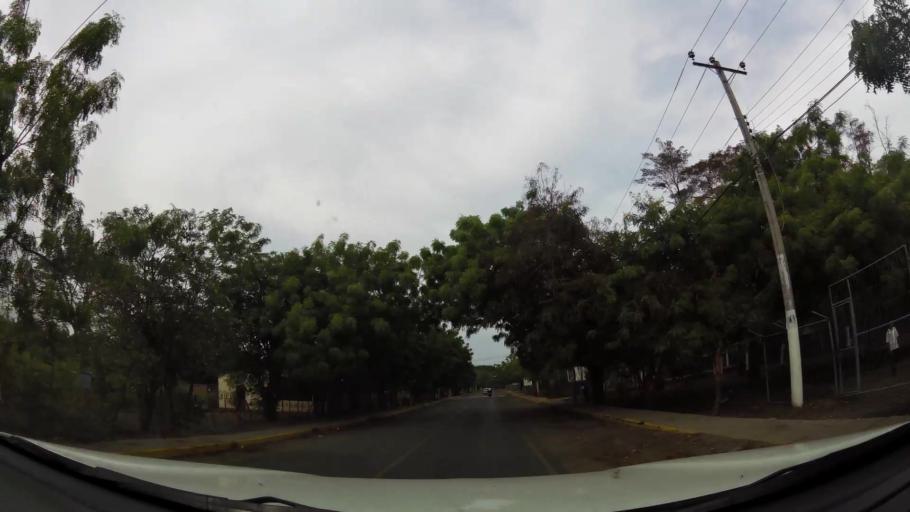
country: NI
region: Rivas
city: San Jorge
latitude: 11.4579
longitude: -85.7960
